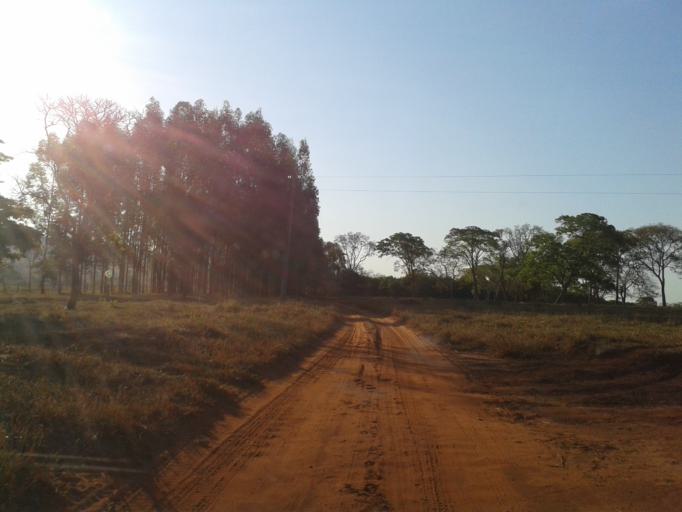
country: BR
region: Minas Gerais
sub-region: Ituiutaba
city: Ituiutaba
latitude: -19.2420
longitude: -49.6026
